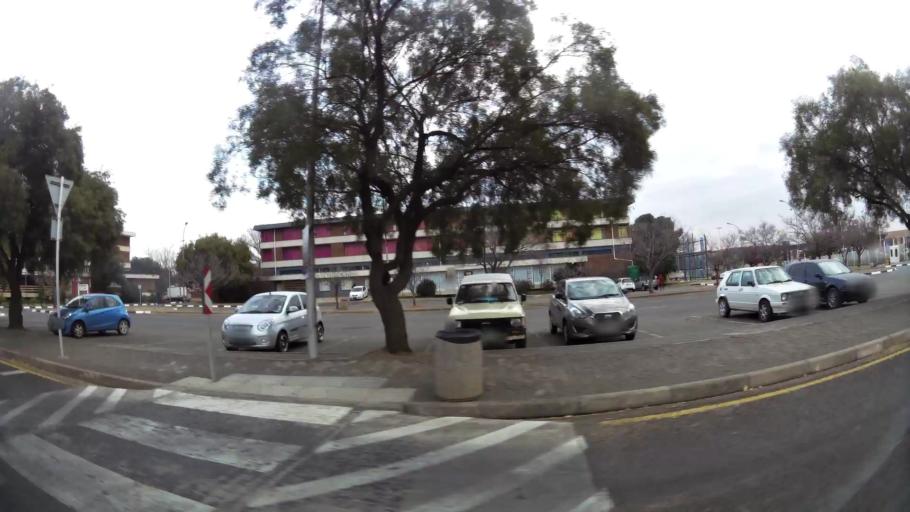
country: ZA
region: Orange Free State
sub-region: Mangaung Metropolitan Municipality
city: Bloemfontein
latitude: -29.1078
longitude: 26.1918
